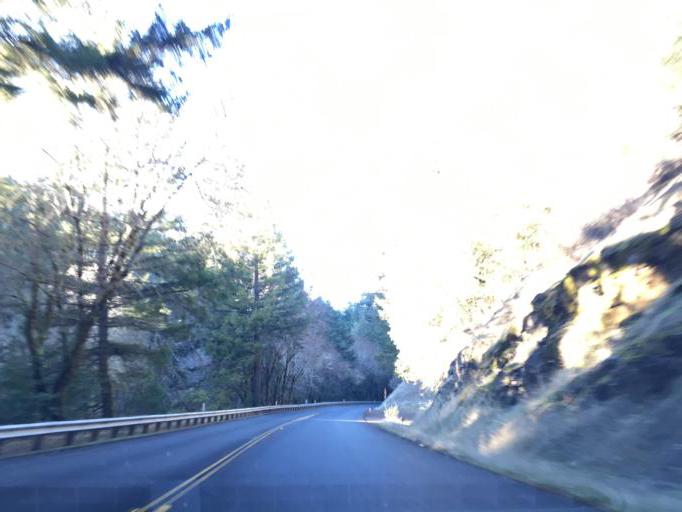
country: US
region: California
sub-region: Mendocino County
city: Laytonville
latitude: 39.8051
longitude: -123.5456
